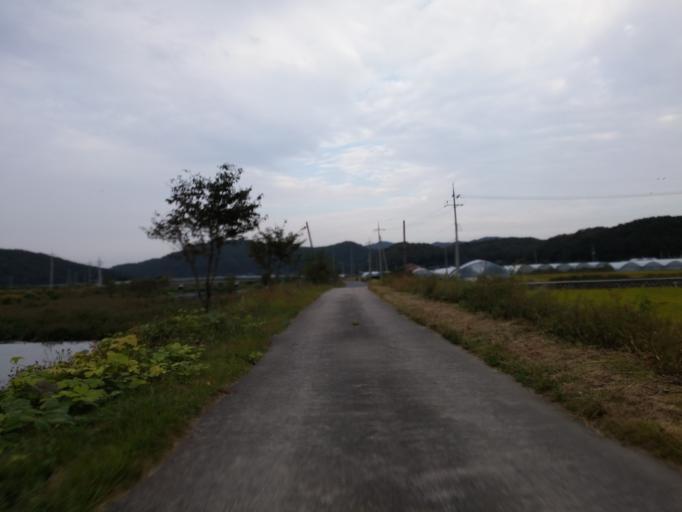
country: KR
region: Daejeon
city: Daejeon
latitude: 36.2456
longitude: 127.3135
